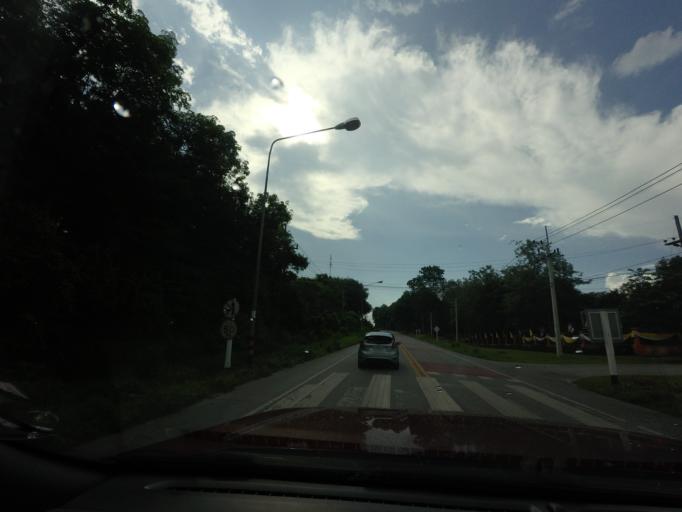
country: TH
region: Pattani
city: Mae Lan
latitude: 6.6664
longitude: 101.1627
